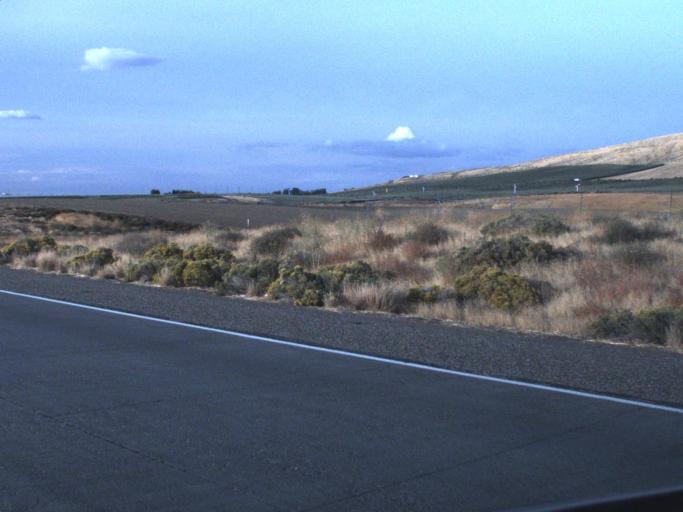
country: US
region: Washington
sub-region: Benton County
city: West Richland
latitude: 46.2217
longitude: -119.3504
